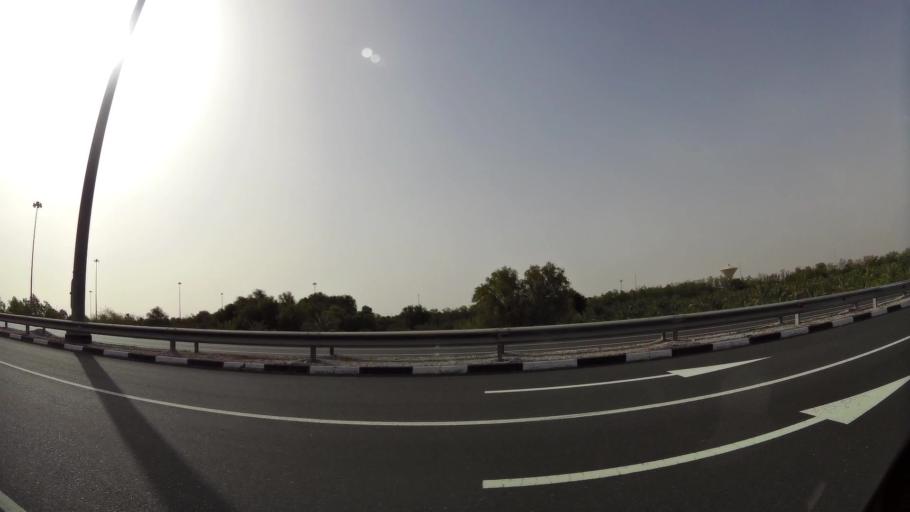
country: AE
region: Abu Dhabi
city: Al Ain
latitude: 24.1847
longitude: 55.5975
